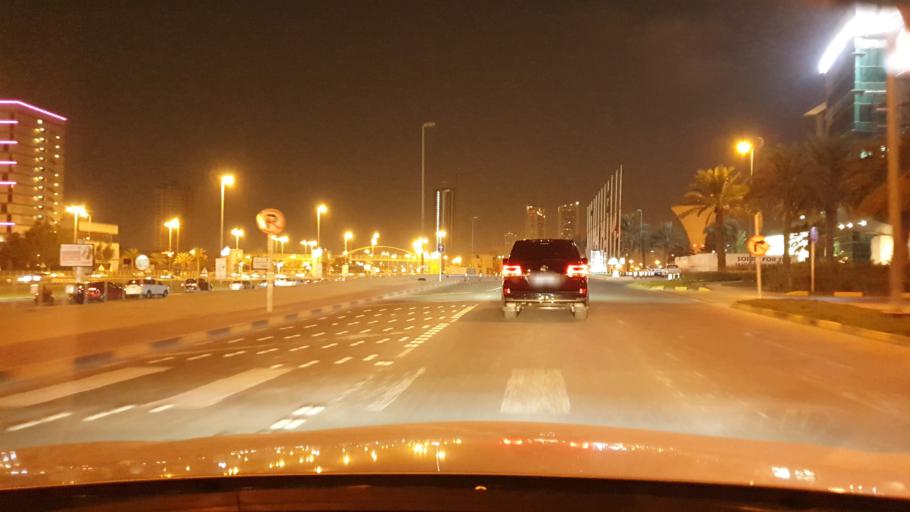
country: BH
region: Manama
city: Manama
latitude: 26.2374
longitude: 50.5749
